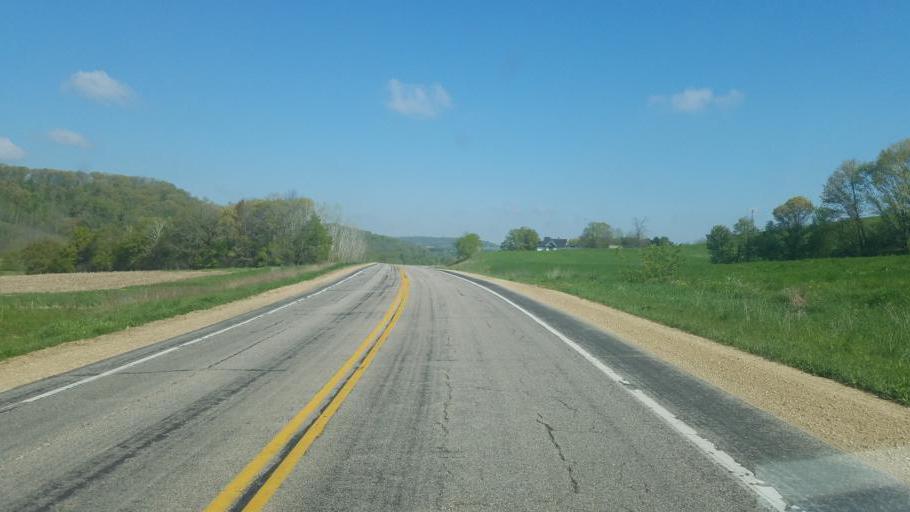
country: US
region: Wisconsin
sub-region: Vernon County
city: Hillsboro
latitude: 43.6111
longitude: -90.3533
